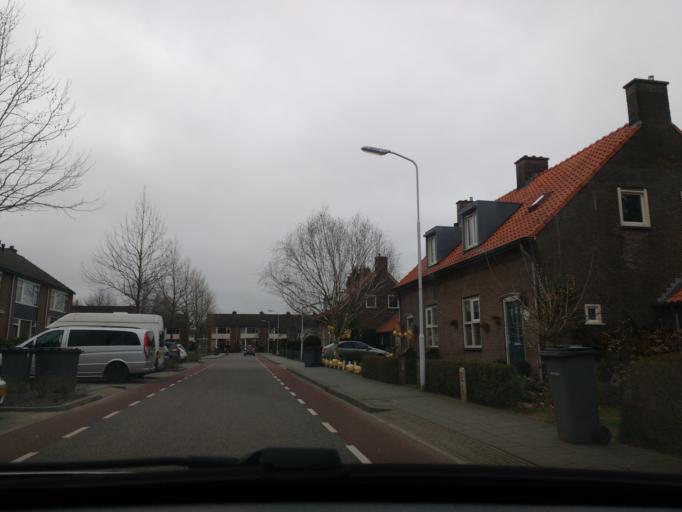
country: NL
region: Gelderland
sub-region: Gemeente Groesbeek
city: Berg en Dal
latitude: 51.8300
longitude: 5.9304
